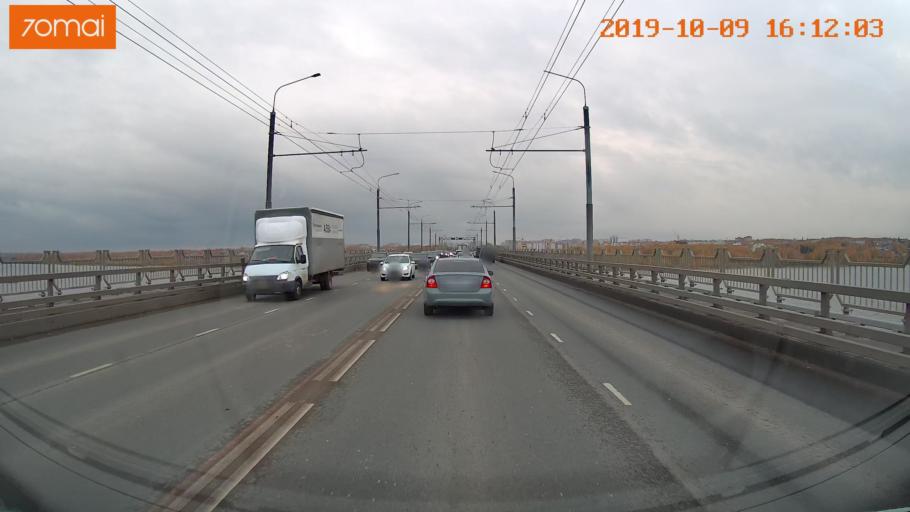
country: RU
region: Kostroma
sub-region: Kostromskoy Rayon
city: Kostroma
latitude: 57.7531
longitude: 40.9396
